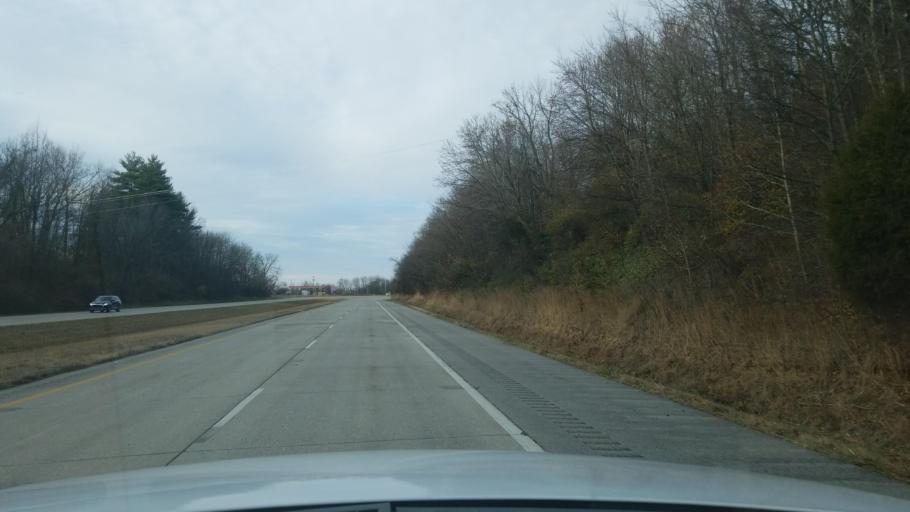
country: US
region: Indiana
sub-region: Vanderburgh County
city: Evansville
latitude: 37.9446
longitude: -87.7124
